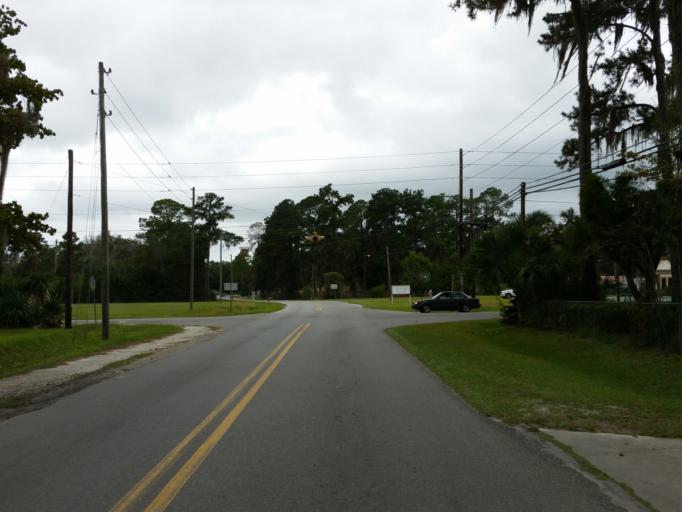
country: US
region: Florida
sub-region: Hamilton County
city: Jasper
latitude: 30.5178
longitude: -82.9593
